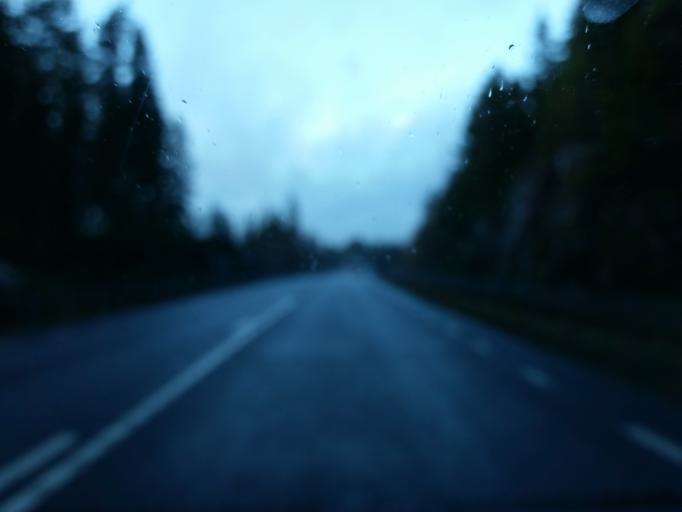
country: SE
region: Joenkoeping
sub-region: Gislaveds Kommun
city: Gislaved
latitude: 57.3306
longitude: 13.5261
